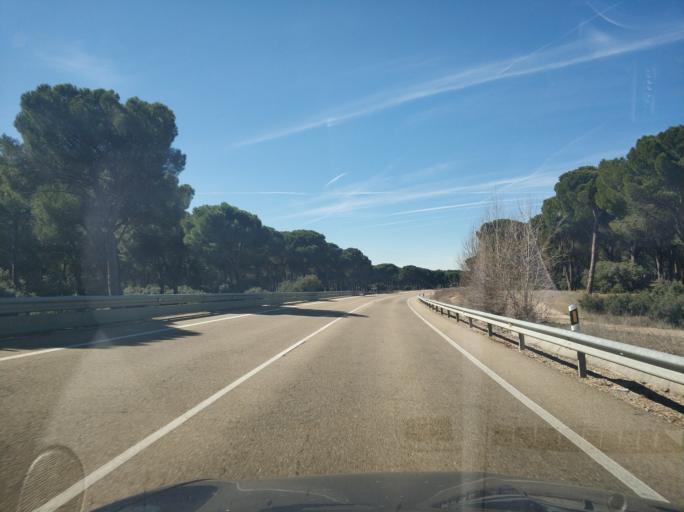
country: ES
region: Castille and Leon
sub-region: Provincia de Valladolid
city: Viana de Cega
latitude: 41.5325
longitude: -4.7475
